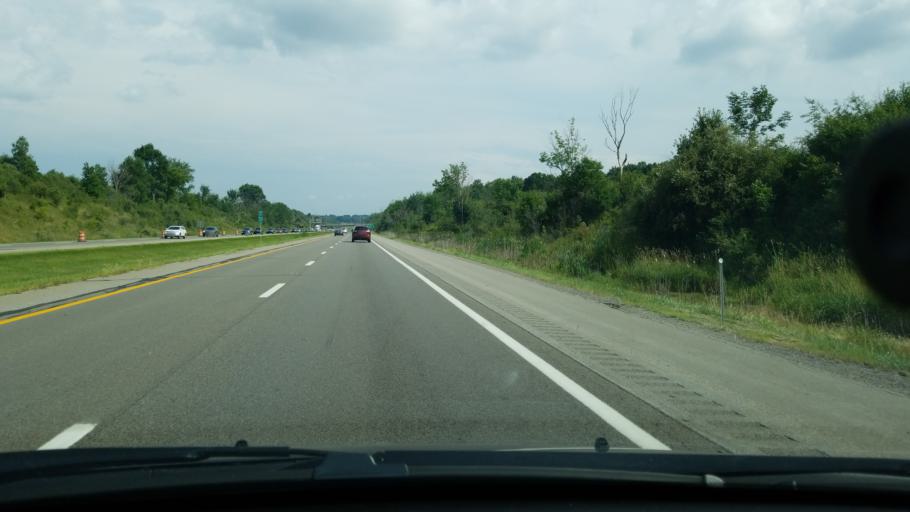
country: US
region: Ohio
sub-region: Mahoning County
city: Boardman
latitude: 40.9630
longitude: -80.6500
